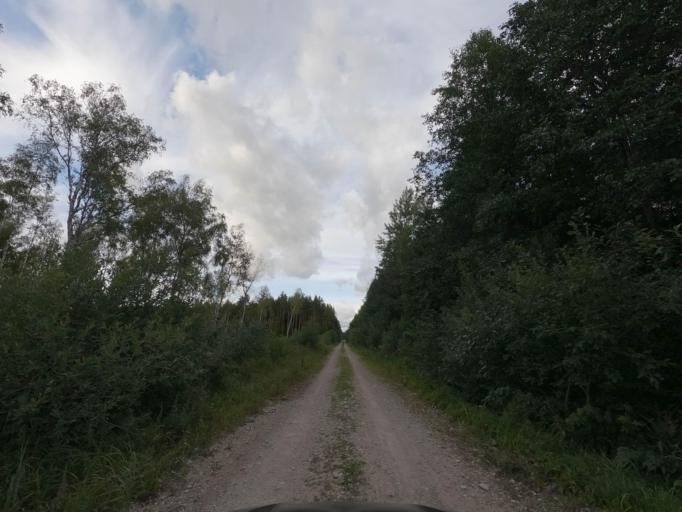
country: EE
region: Raplamaa
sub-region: Rapla vald
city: Rapla
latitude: 59.0062
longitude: 24.7577
